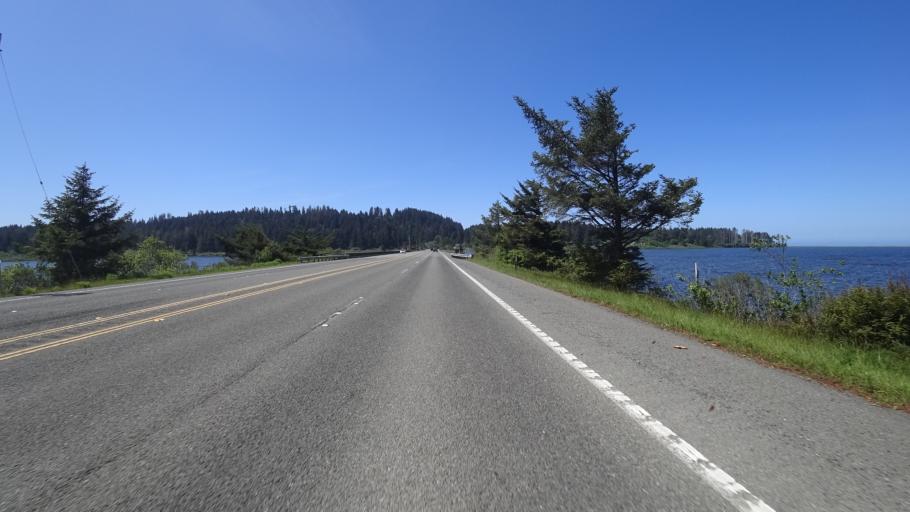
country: US
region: California
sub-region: Humboldt County
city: Westhaven-Moonstone
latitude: 41.1633
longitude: -124.1097
